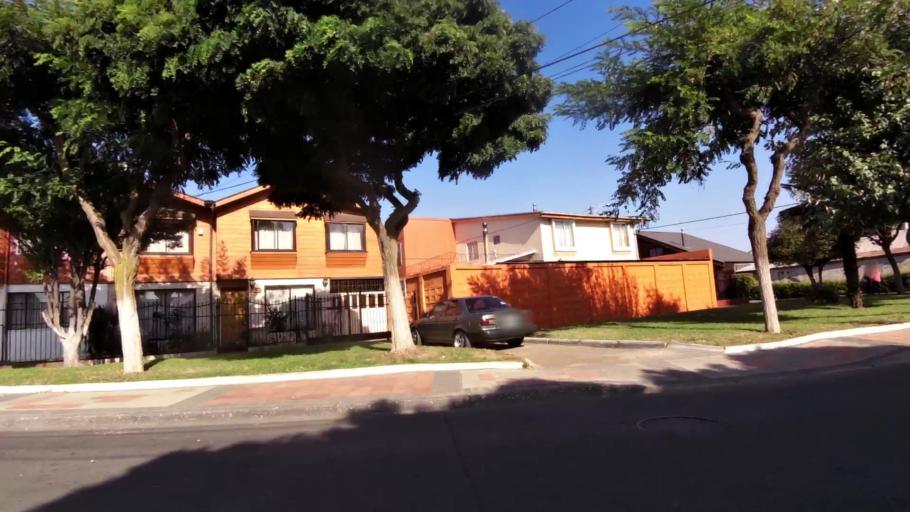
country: CL
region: Biobio
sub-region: Provincia de Concepcion
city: Concepcion
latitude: -36.7967
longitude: -73.0957
